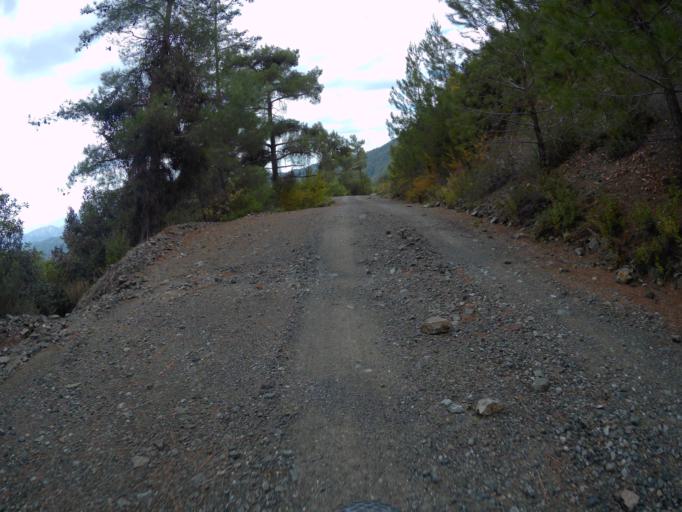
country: CY
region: Lefkosia
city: Kakopetria
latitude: 34.8978
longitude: 32.8483
